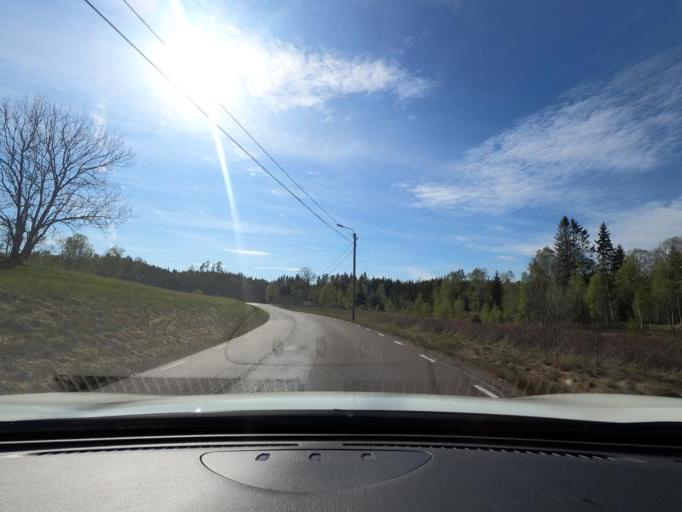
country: SE
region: Vaestra Goetaland
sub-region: Harryda Kommun
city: Landvetter
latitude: 57.6194
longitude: 12.3052
